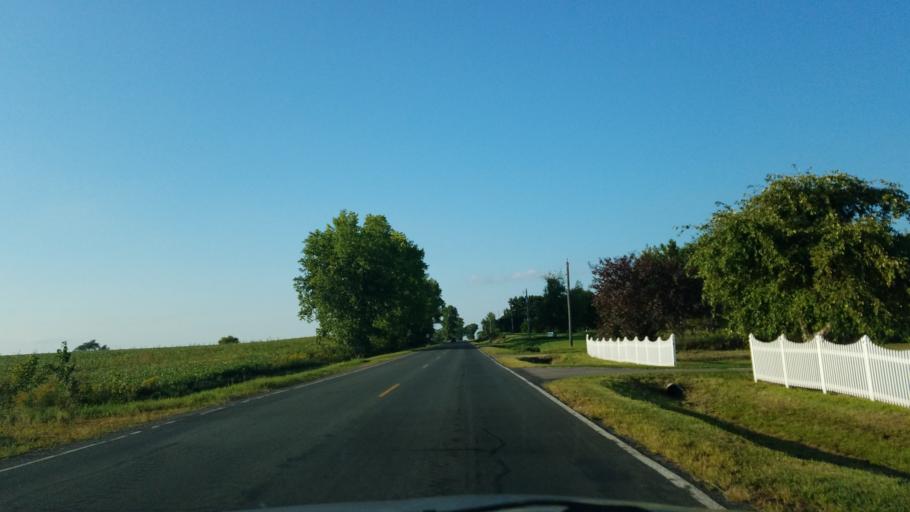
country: US
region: Wisconsin
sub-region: Saint Croix County
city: Roberts
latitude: 44.9970
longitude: -92.5581
